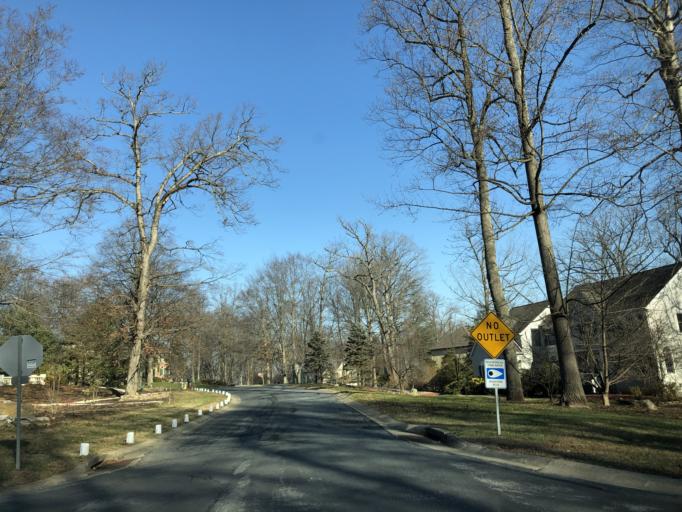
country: US
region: Pennsylvania
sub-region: Chester County
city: Downingtown
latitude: 39.9890
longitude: -75.7010
